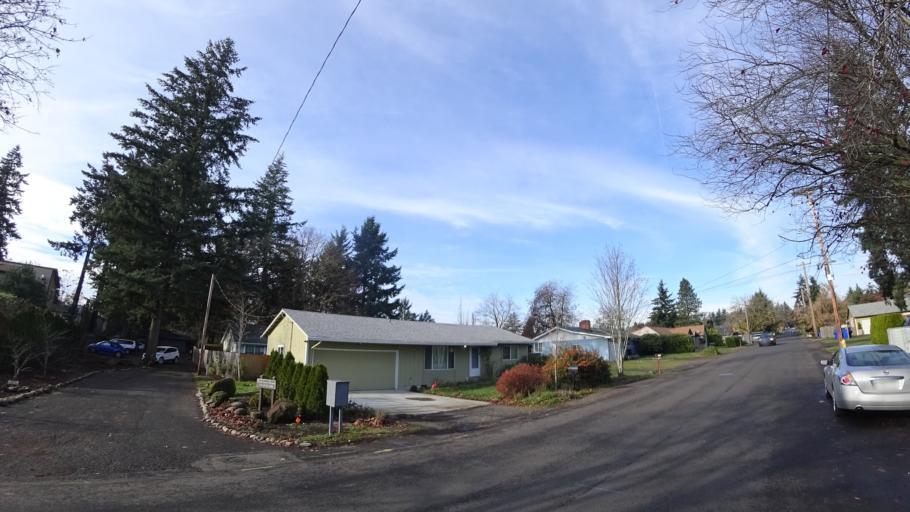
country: US
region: Oregon
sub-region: Multnomah County
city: Lents
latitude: 45.5200
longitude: -122.5210
